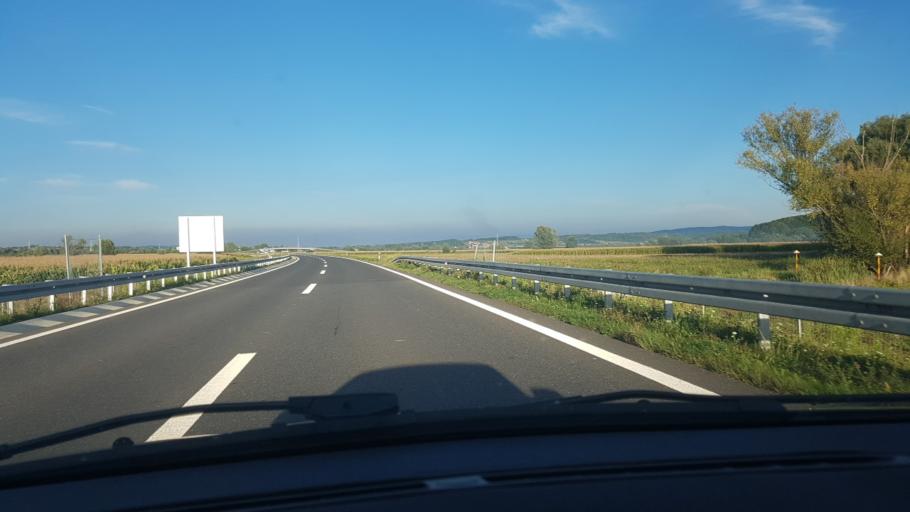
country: HR
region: Krapinsko-Zagorska
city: Selnica
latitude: 46.0393
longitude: 16.0514
